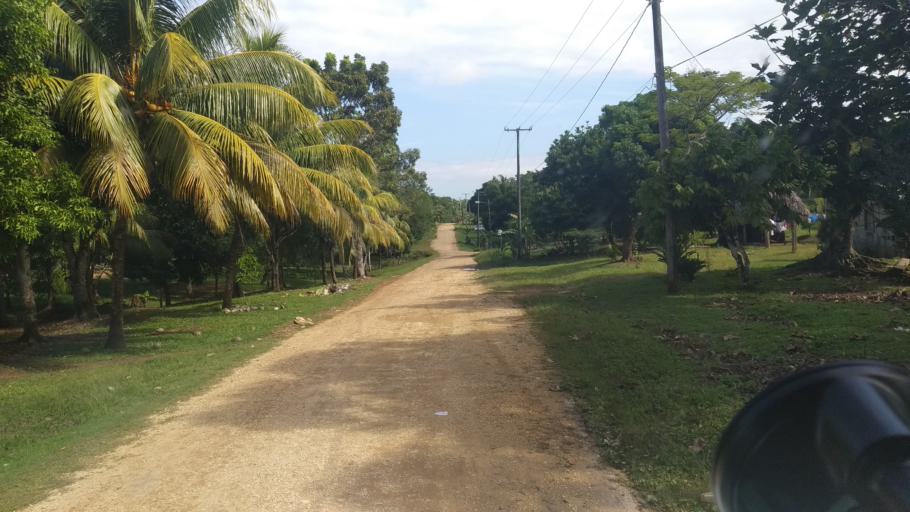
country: BZ
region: Toledo
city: Punta Gorda
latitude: 16.2115
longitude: -88.9116
